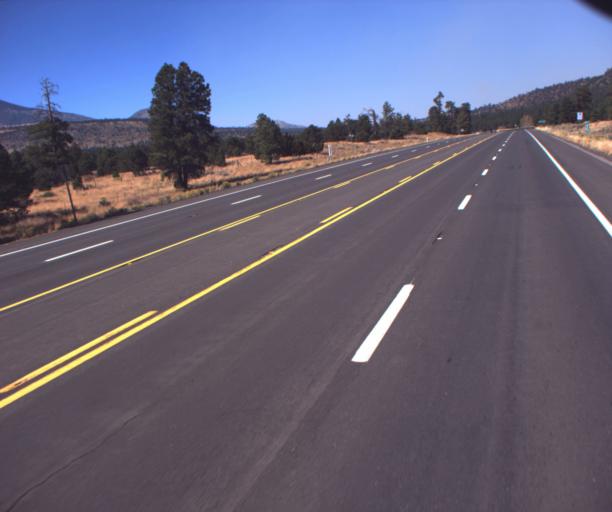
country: US
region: Arizona
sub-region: Coconino County
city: Flagstaff
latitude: 35.3299
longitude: -111.5463
